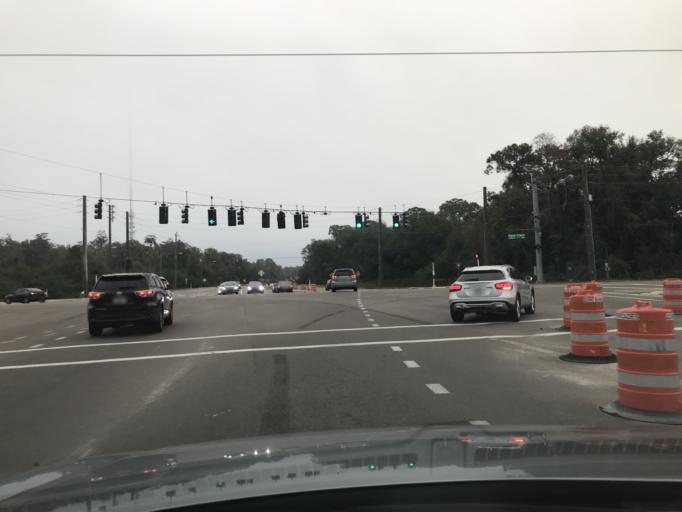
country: US
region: Florida
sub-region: Pinellas County
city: Oldsmar
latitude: 28.0562
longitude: -82.6487
